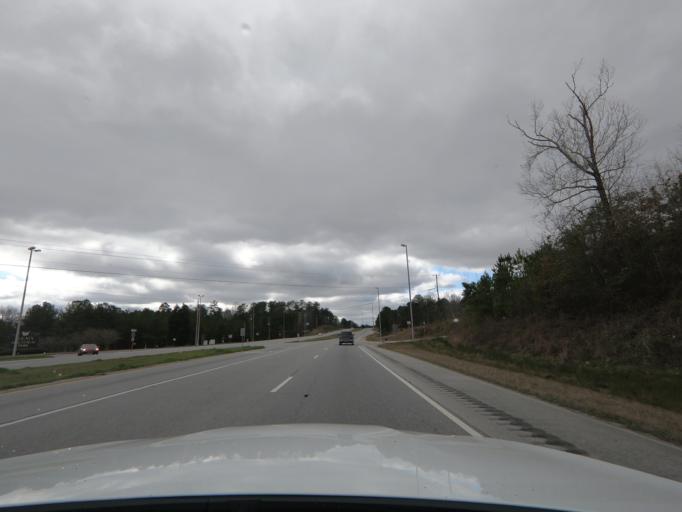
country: US
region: Alabama
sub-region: Russell County
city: Ladonia
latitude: 32.4101
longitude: -85.0487
